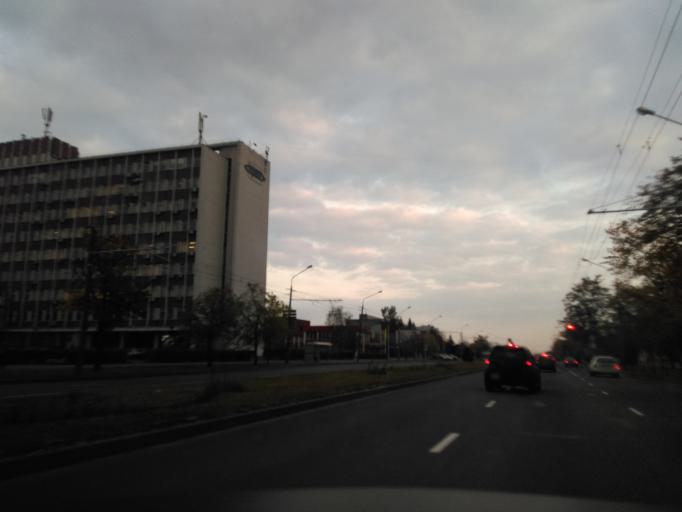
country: BY
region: Minsk
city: Minsk
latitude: 53.8927
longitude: 27.6452
